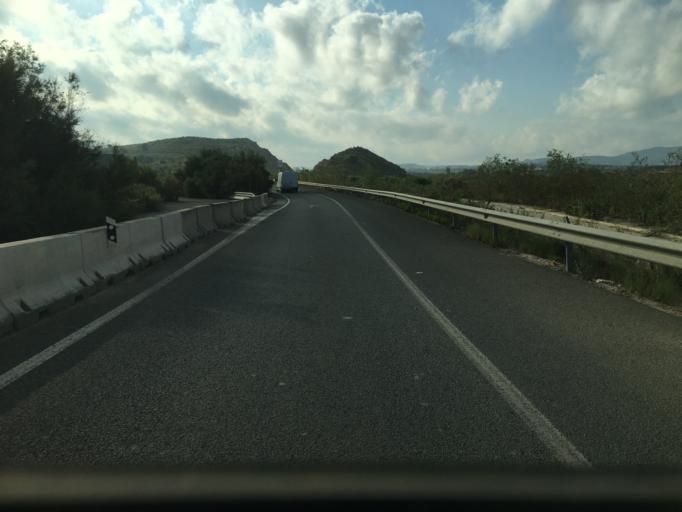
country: ES
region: Murcia
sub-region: Murcia
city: Beniel
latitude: 38.0016
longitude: -1.0138
